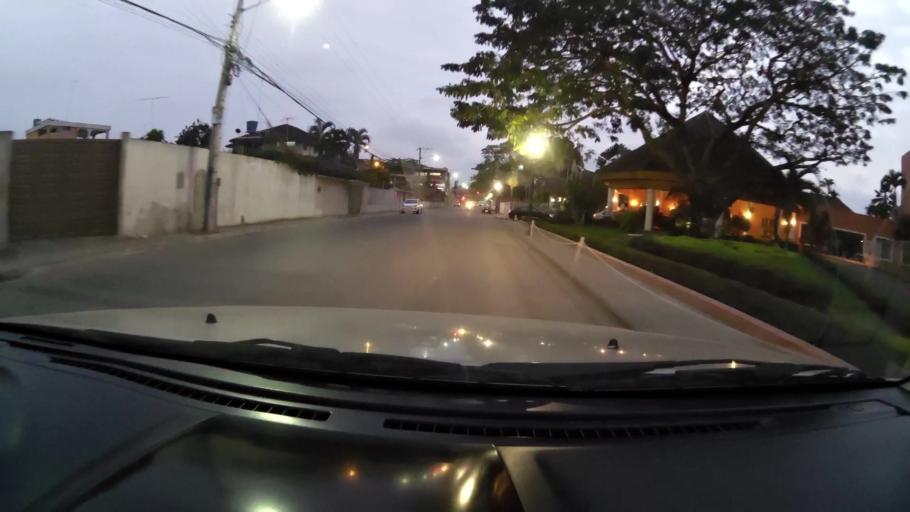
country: EC
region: El Oro
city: Machala
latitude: -3.2623
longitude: -79.9405
